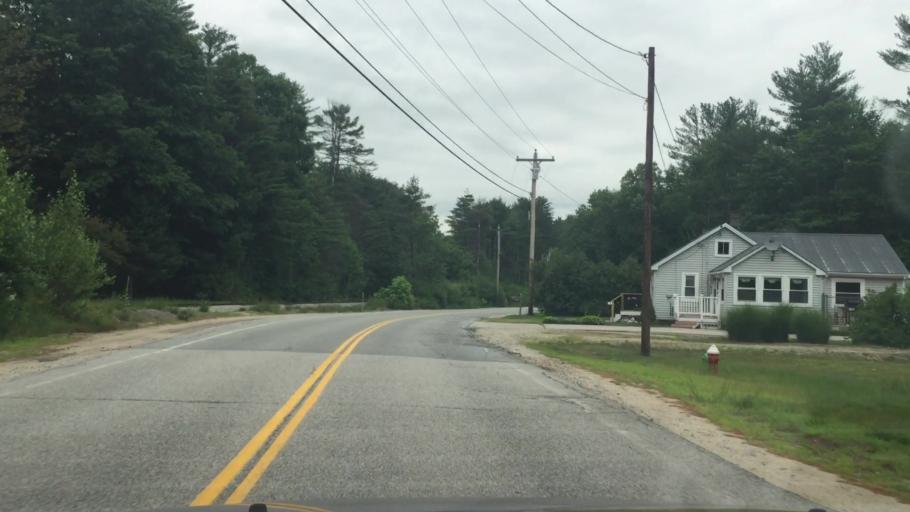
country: US
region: New Hampshire
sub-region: Carroll County
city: North Conway
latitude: 44.0919
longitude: -71.2027
